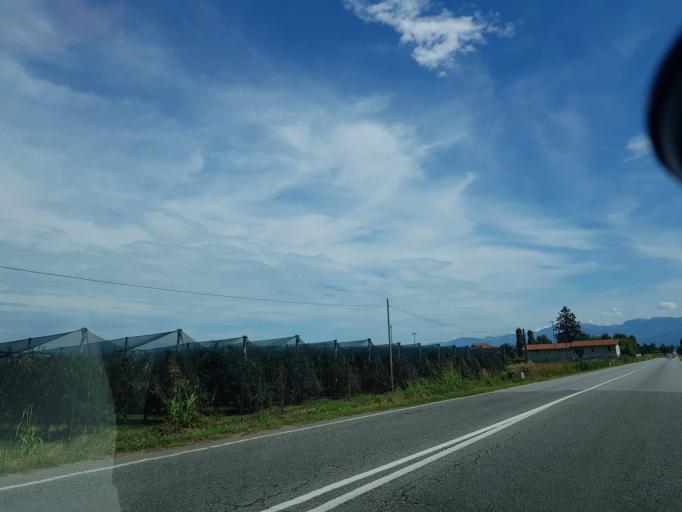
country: IT
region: Piedmont
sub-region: Provincia di Cuneo
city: Roata Rossi
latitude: 44.4707
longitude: 7.5116
